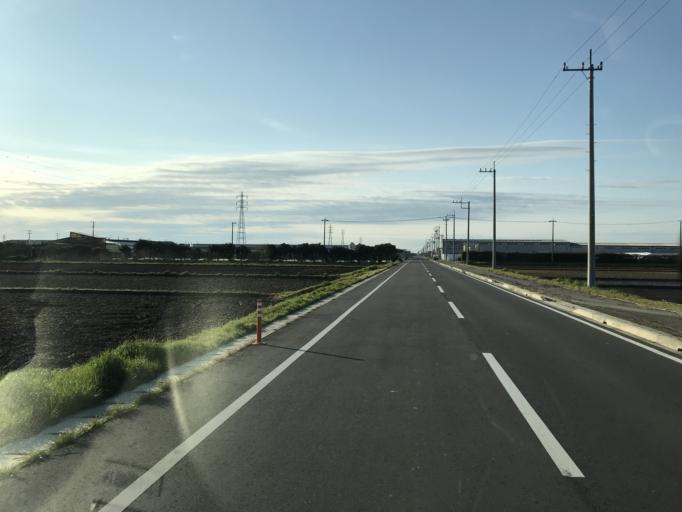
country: JP
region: Chiba
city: Yokaichiba
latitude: 35.6802
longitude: 140.5785
